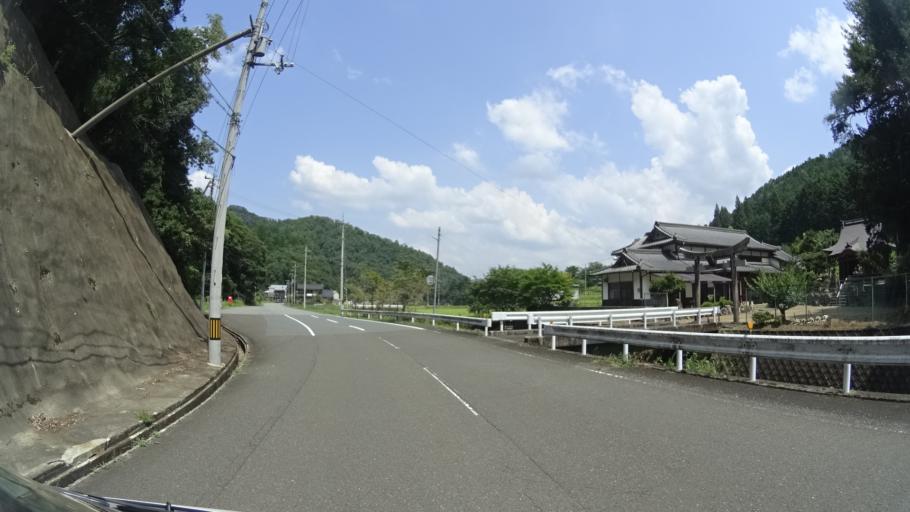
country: JP
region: Kyoto
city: Ayabe
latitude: 35.2096
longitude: 135.2013
